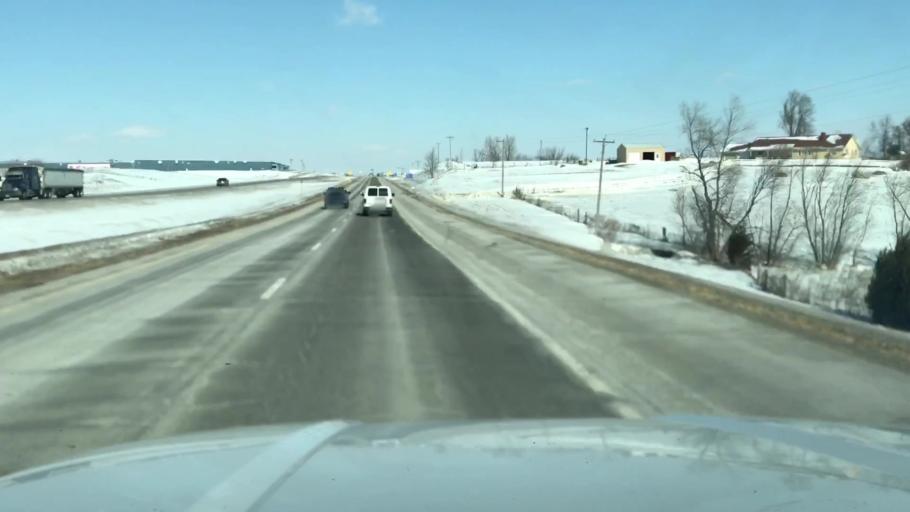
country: US
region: Missouri
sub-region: Nodaway County
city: Maryville
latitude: 40.3039
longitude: -94.8745
